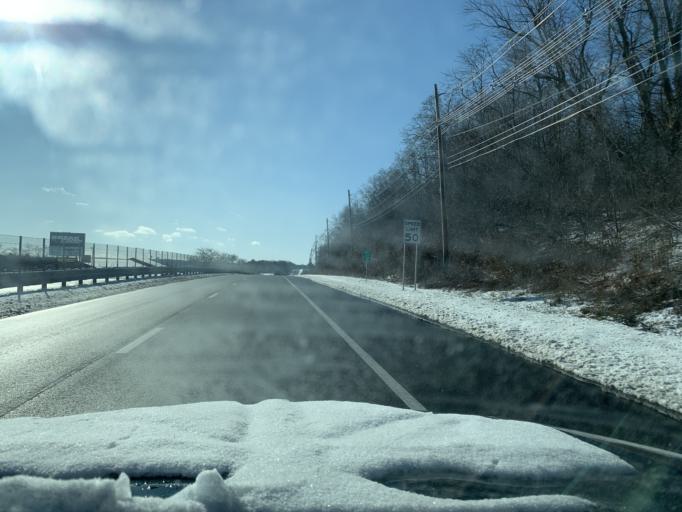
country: US
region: Massachusetts
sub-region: Essex County
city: Danvers
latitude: 42.5798
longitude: -70.9690
